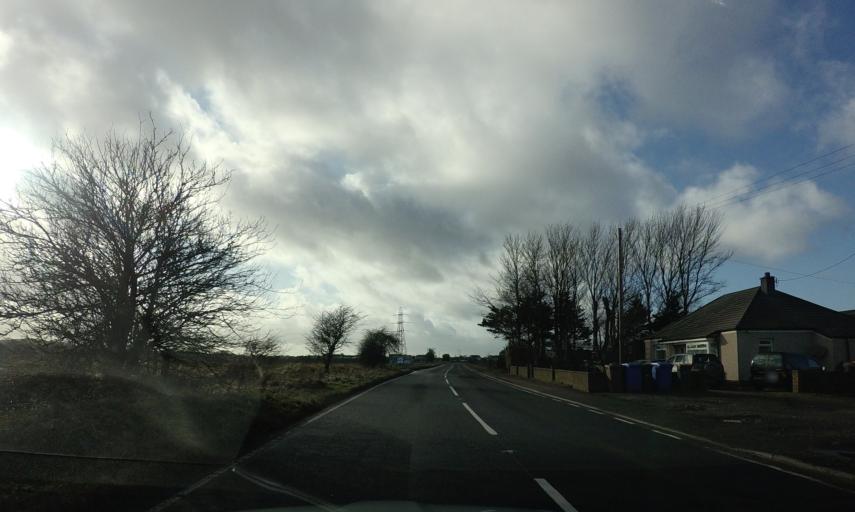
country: GB
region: Scotland
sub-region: West Lothian
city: Kirknewton
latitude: 55.9004
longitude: -3.4239
